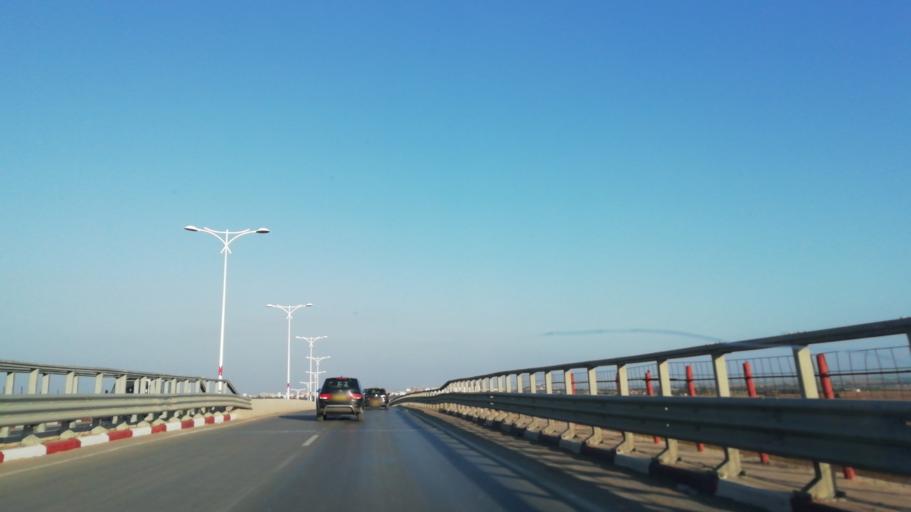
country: DZ
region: Sidi Bel Abbes
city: Sidi Bel Abbes
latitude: 35.1690
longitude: -0.6840
